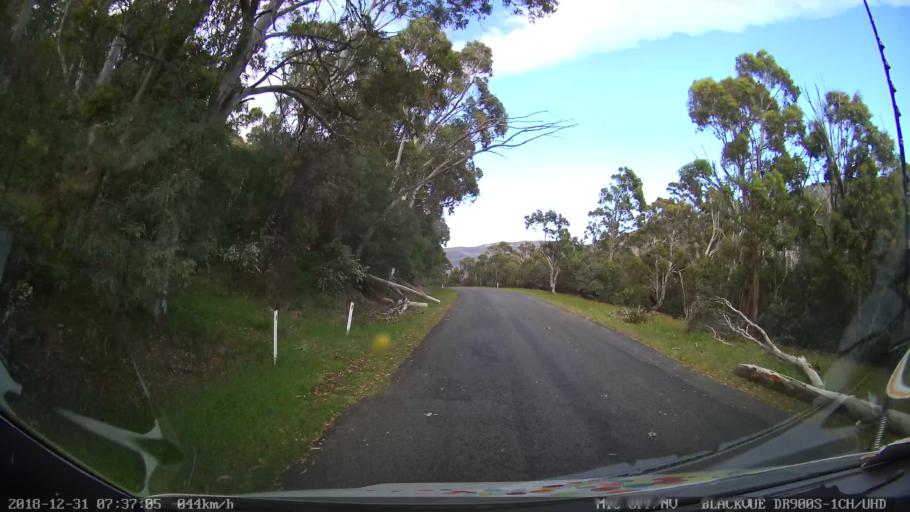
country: AU
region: New South Wales
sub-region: Snowy River
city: Jindabyne
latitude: -36.3437
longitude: 148.4390
